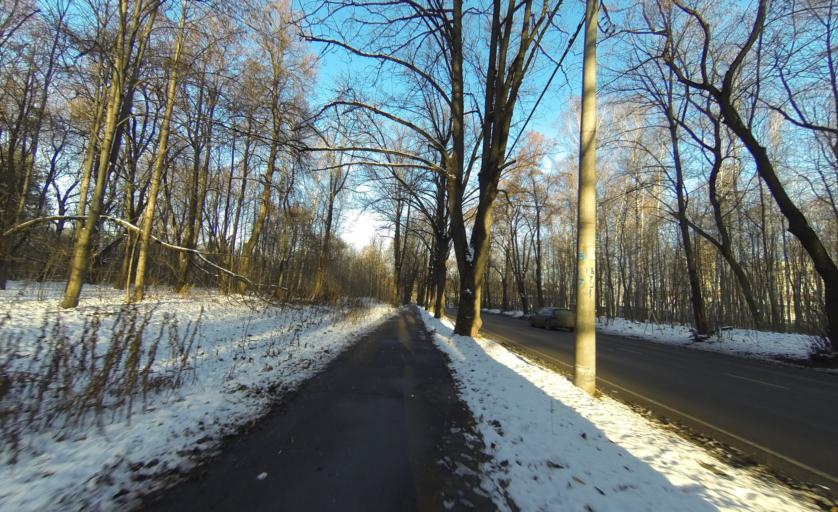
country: RU
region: Moscow
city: Sokol'niki
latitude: 55.8139
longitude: 37.6841
